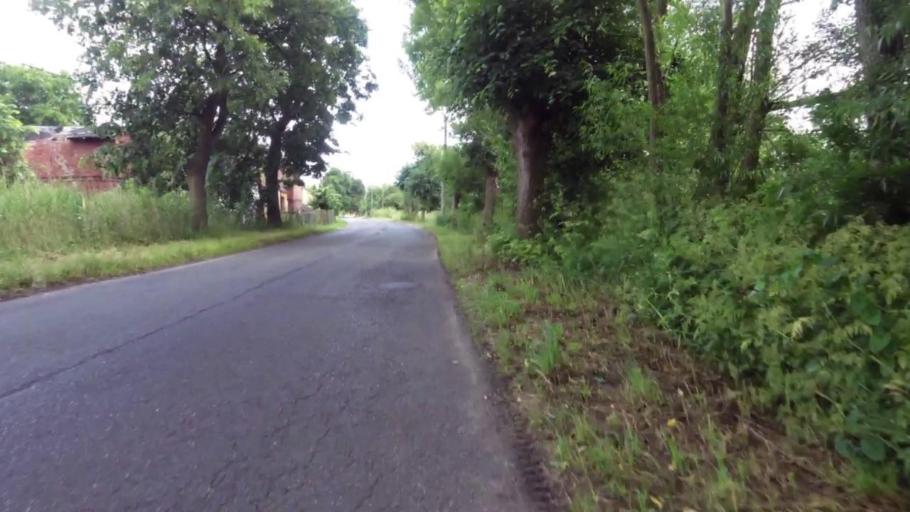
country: PL
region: West Pomeranian Voivodeship
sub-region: Powiat goleniowski
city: Stepnica
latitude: 53.6607
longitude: 14.6104
